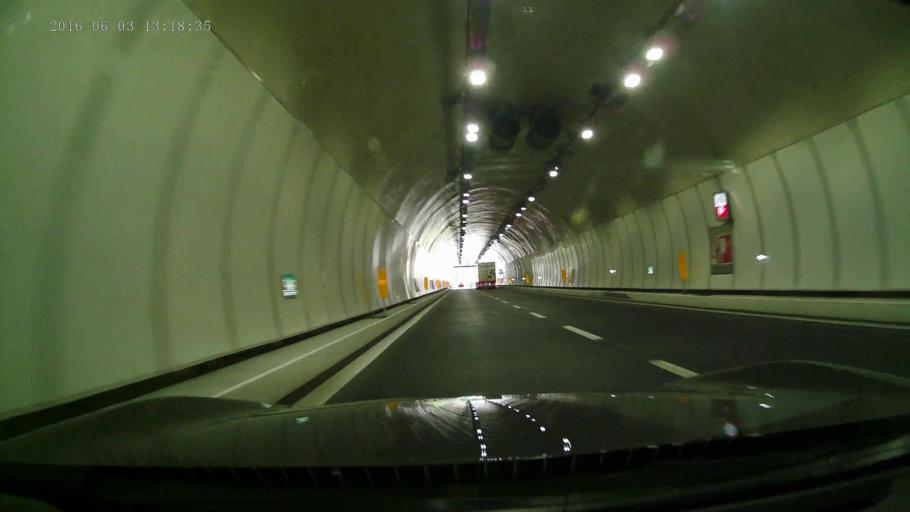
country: IT
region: Trentino-Alto Adige
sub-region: Bolzano
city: Ponte Gardena
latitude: 46.5594
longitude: 11.5129
